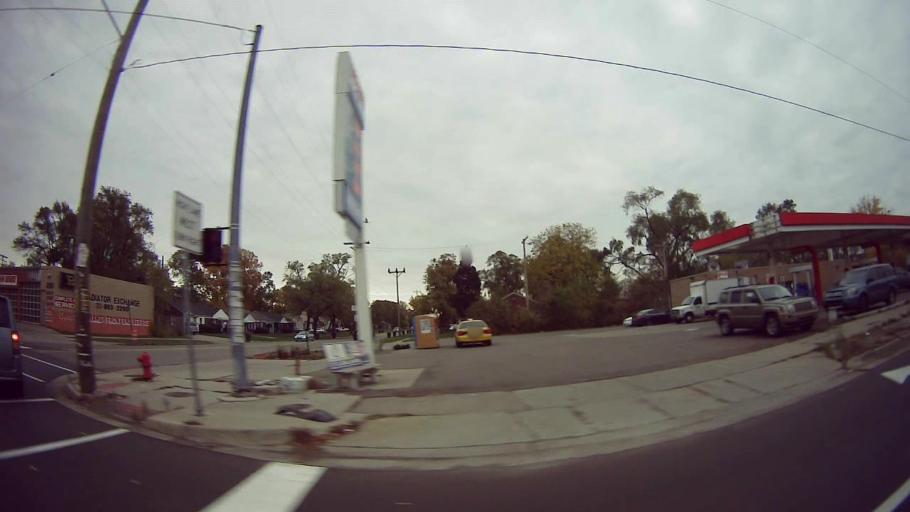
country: US
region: Michigan
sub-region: Oakland County
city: Oak Park
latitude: 42.4454
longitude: -83.1722
